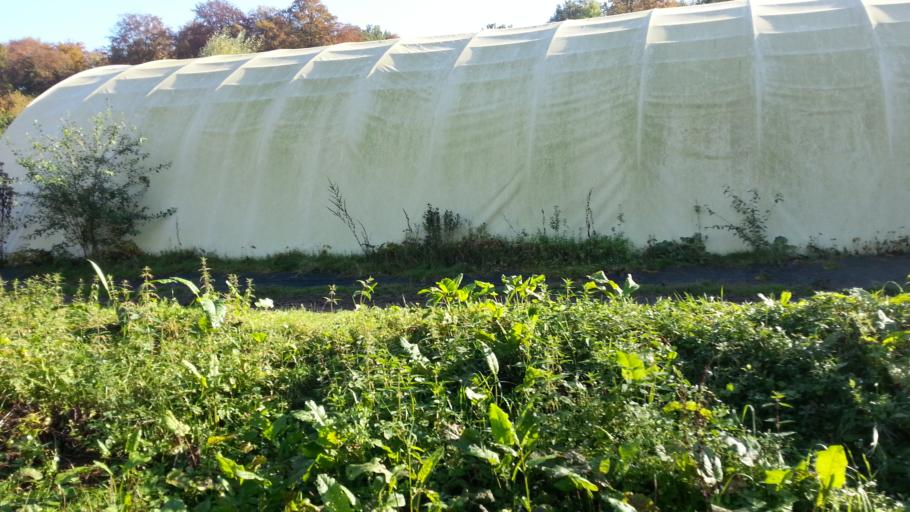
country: FR
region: Picardie
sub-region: Departement de l'Oise
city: Balagny-sur-Therain
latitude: 49.2849
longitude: 2.3475
